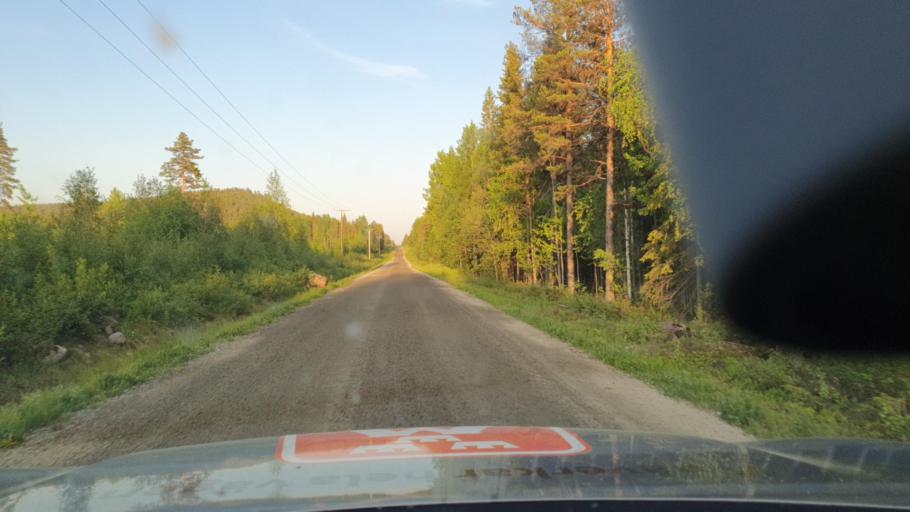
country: SE
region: Norrbotten
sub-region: Bodens Kommun
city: Boden
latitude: 66.0745
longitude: 21.6988
